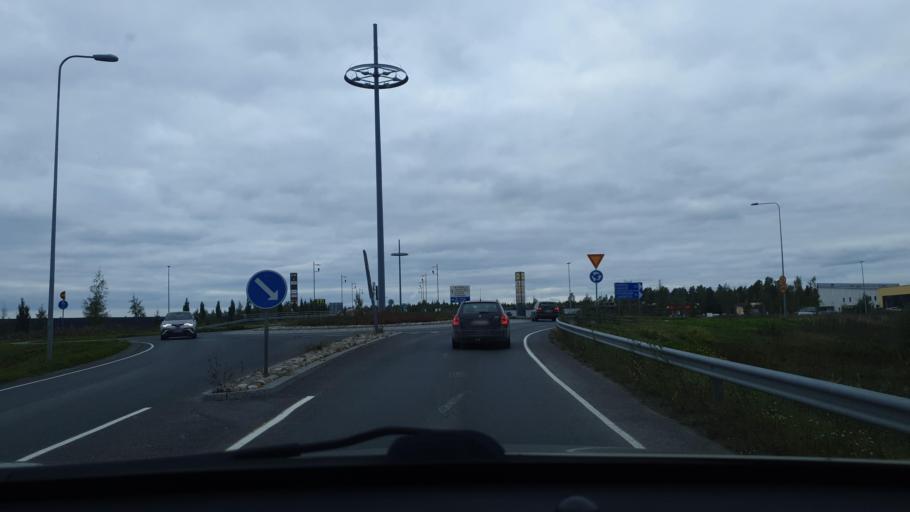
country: FI
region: Ostrobothnia
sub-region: Vaasa
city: Korsholm
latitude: 63.1111
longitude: 21.6625
